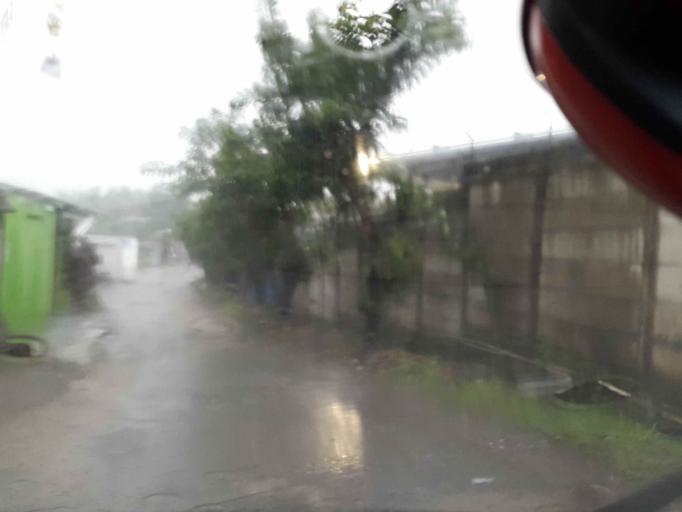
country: ID
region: West Java
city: Cimahi
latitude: -6.8990
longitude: 107.4962
